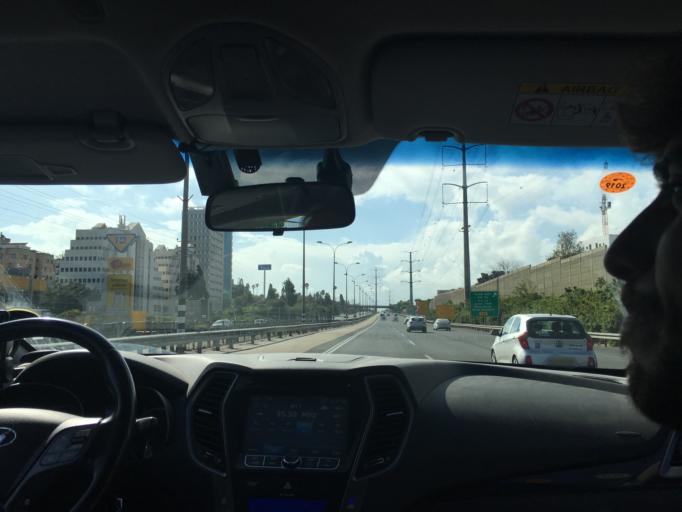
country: IL
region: Tel Aviv
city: Giv`at Shemu'el
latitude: 32.0824
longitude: 34.8452
